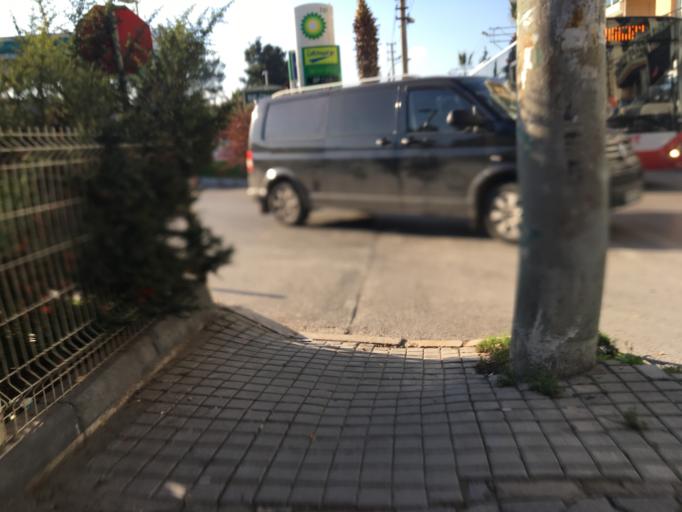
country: TR
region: Izmir
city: Buca
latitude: 38.3830
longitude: 27.1717
